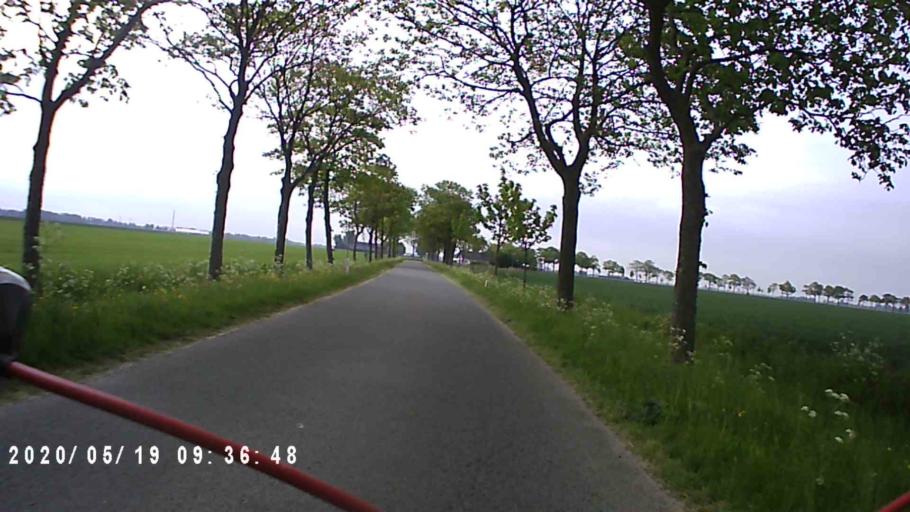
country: NL
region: Groningen
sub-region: Gemeente Zuidhorn
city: Grijpskerk
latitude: 53.2921
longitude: 6.2836
